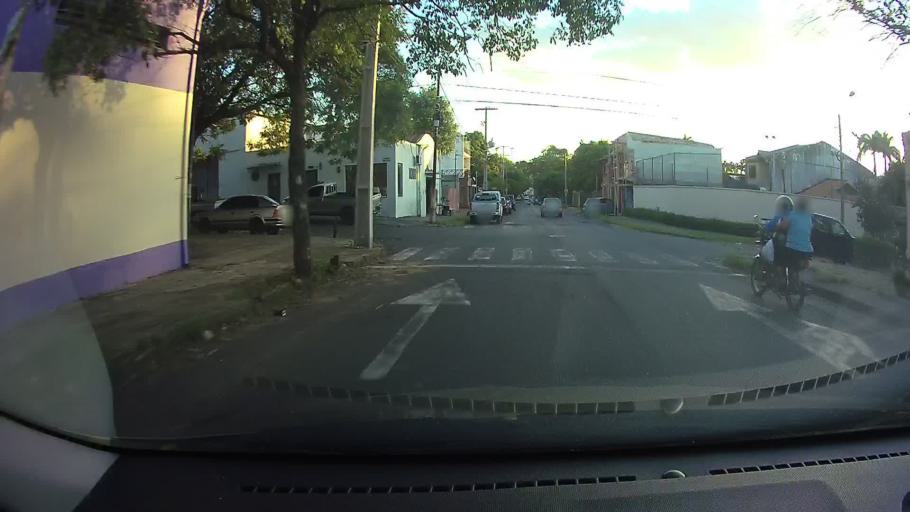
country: PY
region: Central
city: Lambare
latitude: -25.3108
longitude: -57.5791
